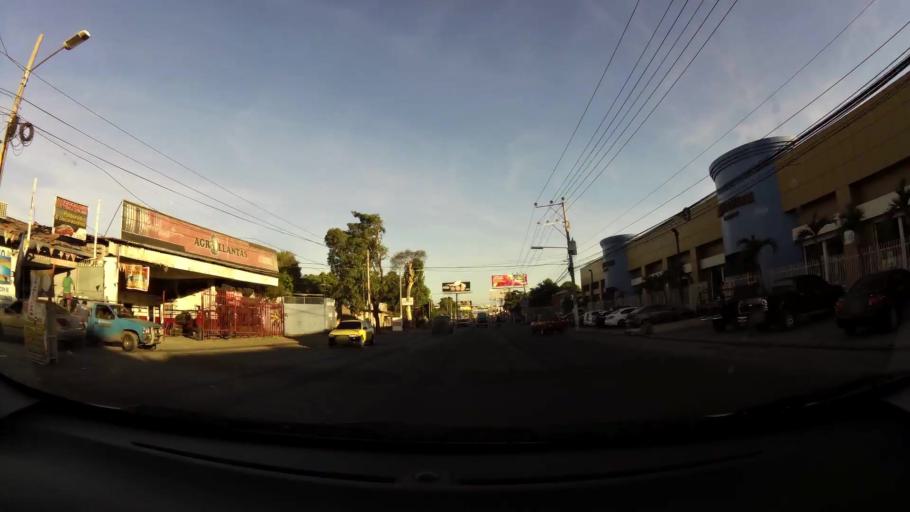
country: SV
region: San Miguel
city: San Miguel
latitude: 13.4648
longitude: -88.1704
